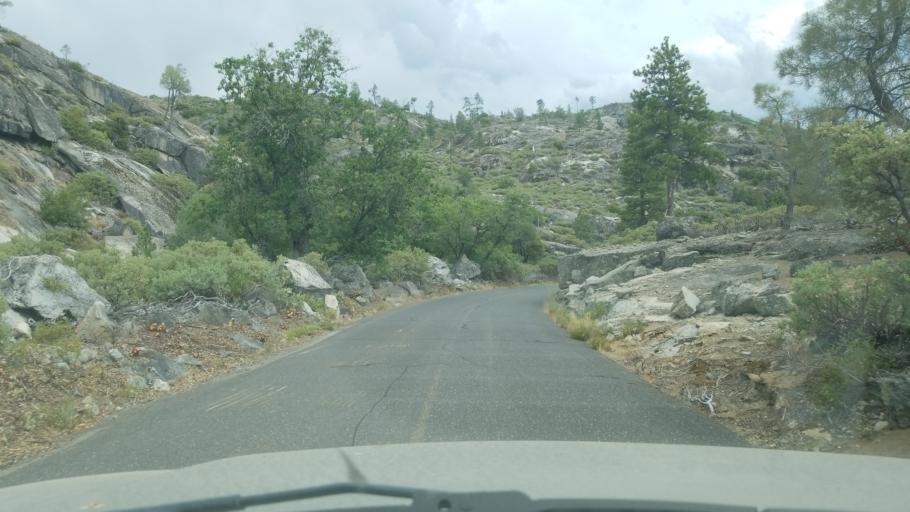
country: US
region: California
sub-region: Mariposa County
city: Yosemite Valley
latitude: 37.9011
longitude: -119.8364
